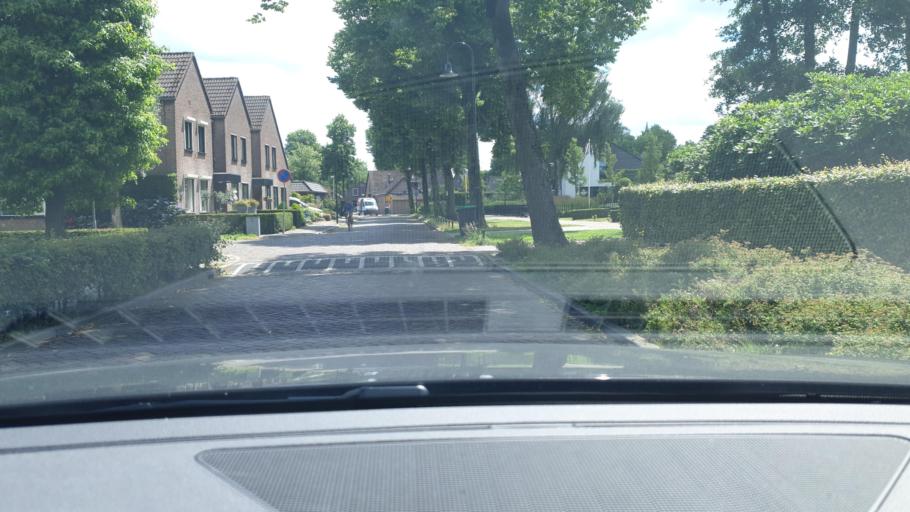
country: NL
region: North Brabant
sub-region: Gemeente Uden
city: Uden
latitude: 51.6578
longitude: 5.6058
